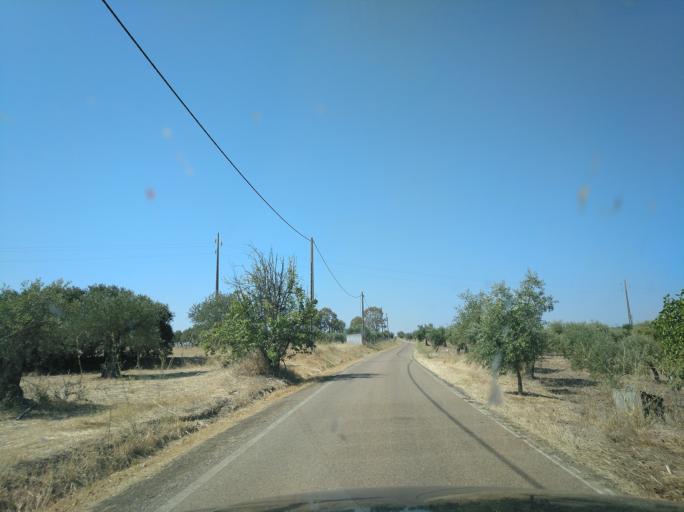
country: PT
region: Portalegre
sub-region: Campo Maior
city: Campo Maior
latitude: 39.0317
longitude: -7.0446
